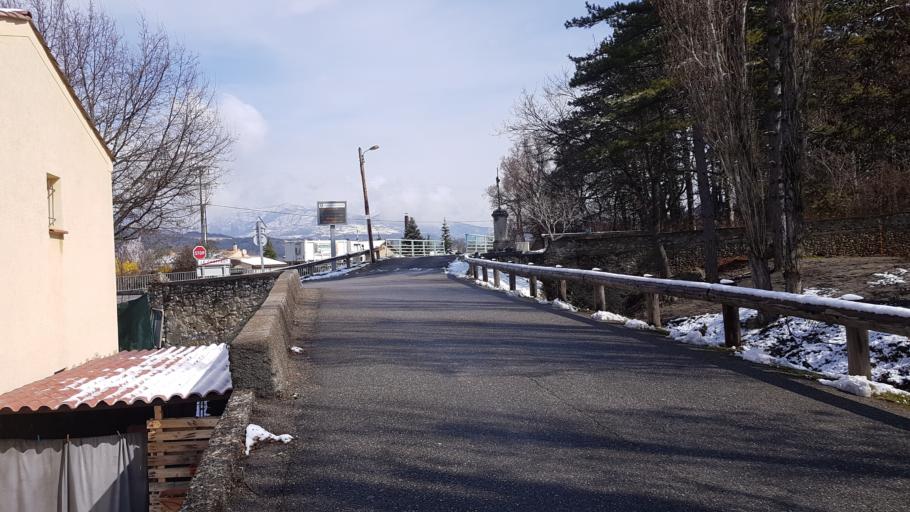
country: FR
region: Provence-Alpes-Cote d'Azur
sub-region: Departement des Alpes-de-Haute-Provence
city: Mallemoisson
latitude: 44.0392
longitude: 6.1512
